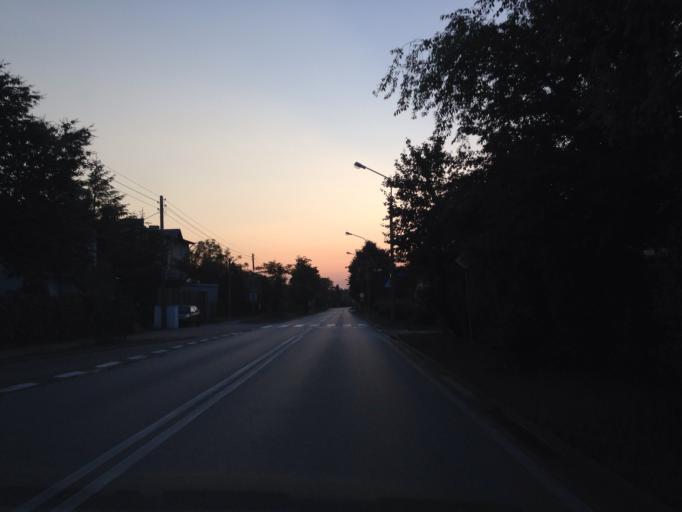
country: PL
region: Masovian Voivodeship
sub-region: Powiat warszawski zachodni
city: Babice
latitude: 52.2483
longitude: 20.8788
